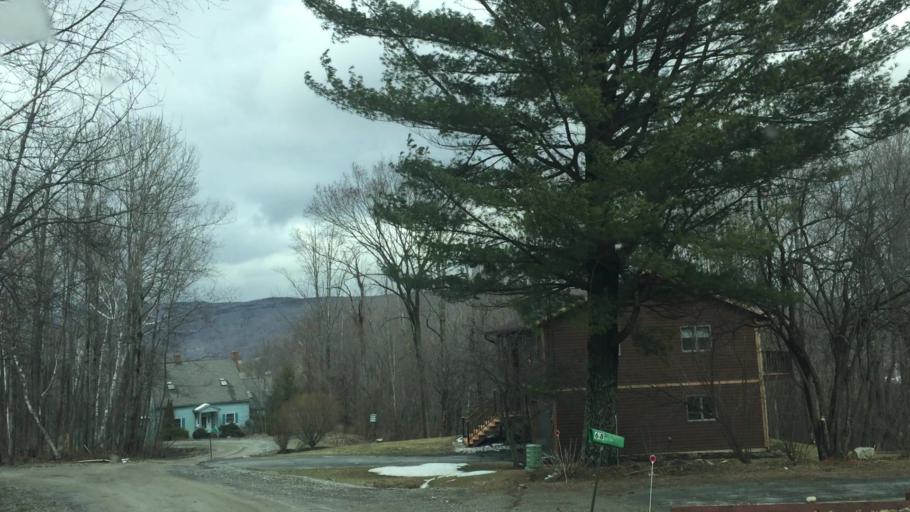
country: US
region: Massachusetts
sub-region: Berkshire County
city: Lanesborough
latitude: 42.5411
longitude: -73.2420
